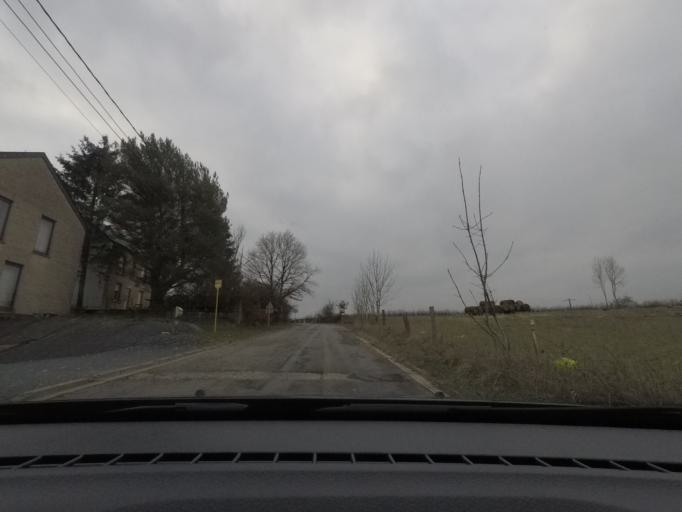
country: BE
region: Wallonia
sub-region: Province du Luxembourg
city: Habay-la-Vieille
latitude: 49.7150
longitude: 5.5817
